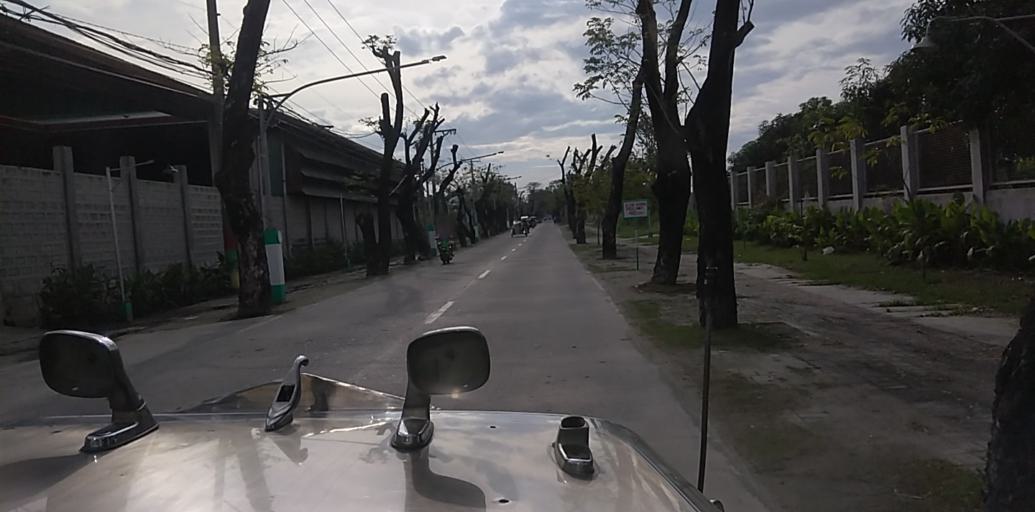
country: PH
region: Central Luzon
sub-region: Province of Pampanga
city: Minalin
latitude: 14.9824
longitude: 120.6987
